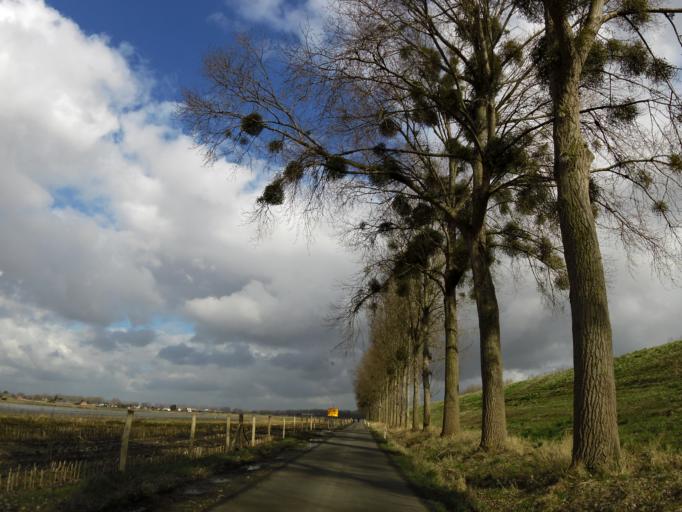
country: NL
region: Limburg
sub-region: Gemeente Stein
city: Elsloo
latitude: 50.9388
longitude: 5.7491
